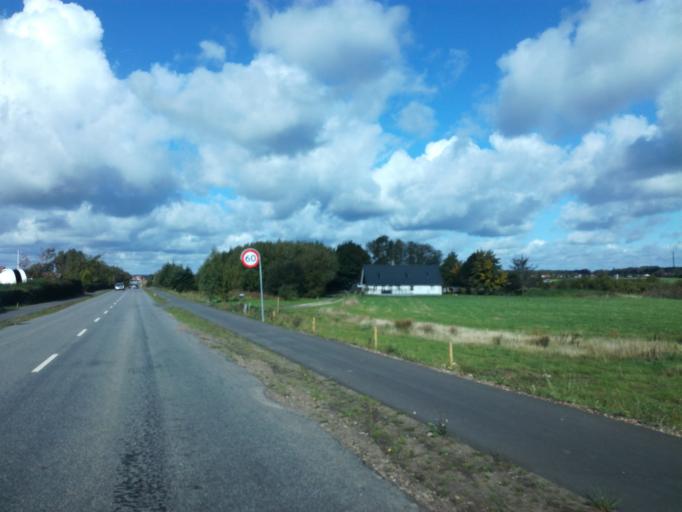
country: DK
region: South Denmark
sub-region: Fredericia Kommune
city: Fredericia
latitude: 55.6089
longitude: 9.7529
